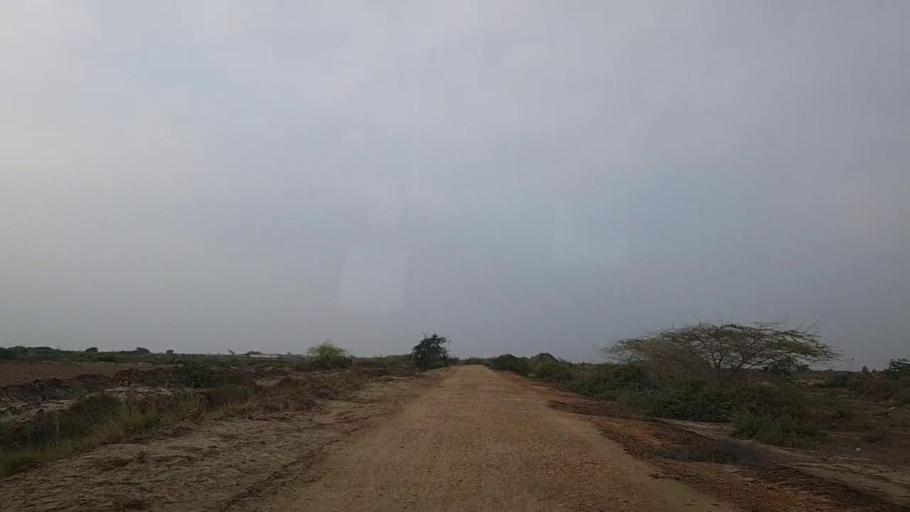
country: PK
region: Sindh
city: Mirpur Sakro
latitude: 24.6118
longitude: 67.5154
